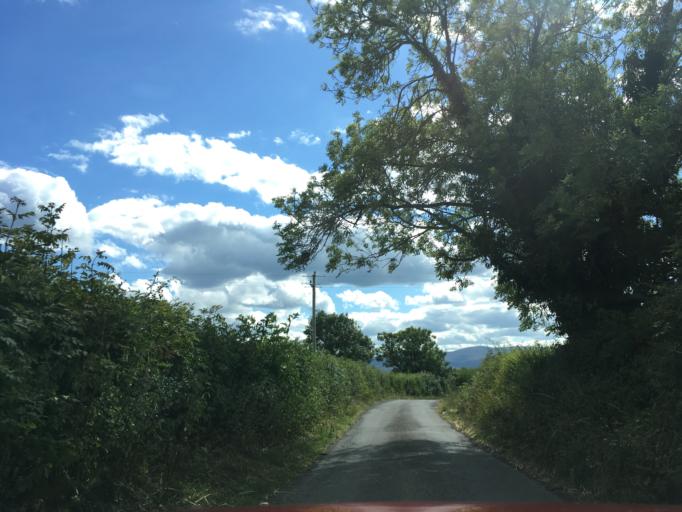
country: IE
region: Munster
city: Cashel
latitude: 52.4846
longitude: -7.9655
